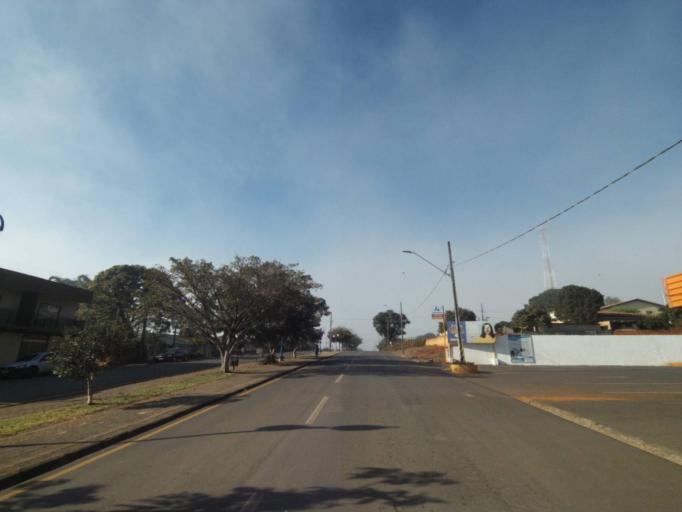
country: BR
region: Parana
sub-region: Tibagi
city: Tibagi
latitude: -24.5212
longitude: -50.4110
